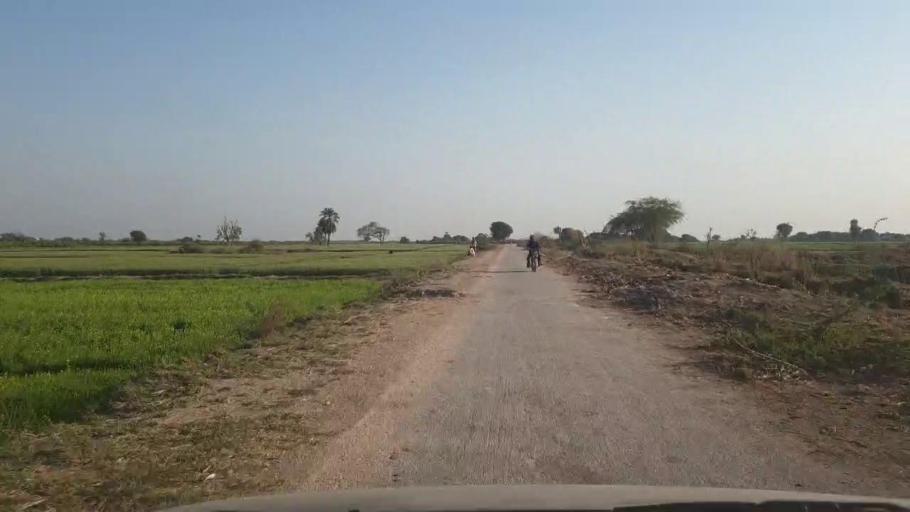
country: PK
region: Sindh
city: Chambar
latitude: 25.2595
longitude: 68.8875
